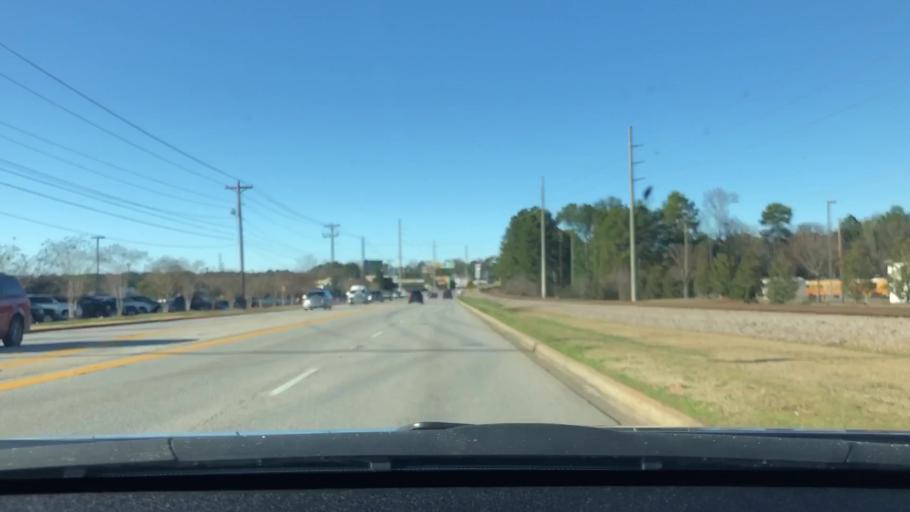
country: US
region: South Carolina
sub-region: Lexington County
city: Irmo
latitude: 34.0692
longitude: -81.1726
